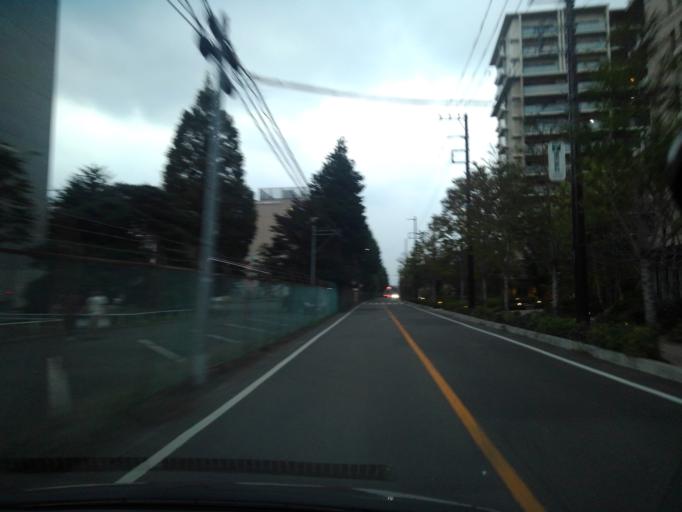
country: JP
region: Tokyo
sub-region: Machida-shi
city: Machida
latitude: 35.5747
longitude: 139.3924
